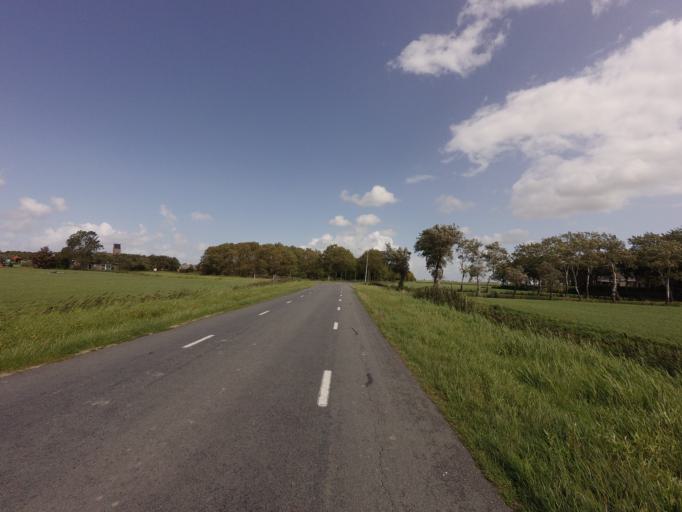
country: NL
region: Friesland
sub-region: Gemeente Harlingen
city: Harlingen
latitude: 53.1117
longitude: 5.4397
